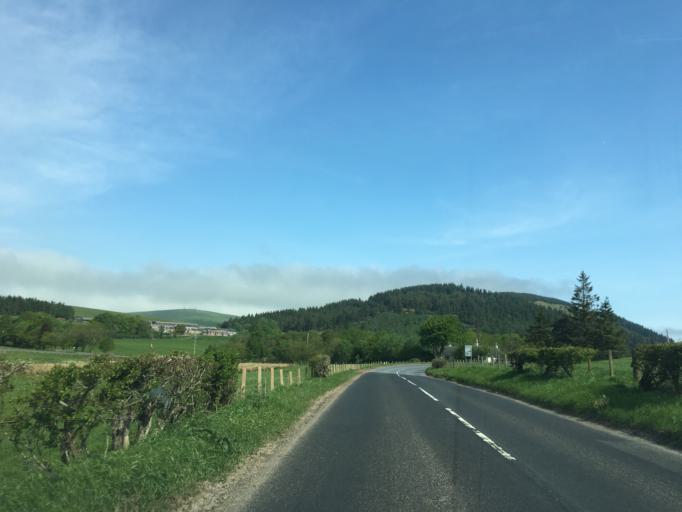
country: GB
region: Scotland
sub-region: South Lanarkshire
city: Biggar
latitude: 55.6517
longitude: -3.4336
